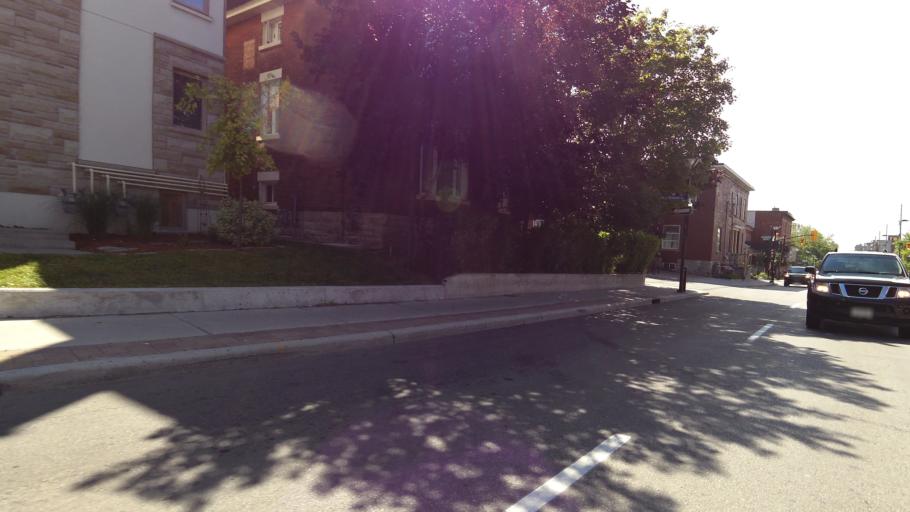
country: CA
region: Ontario
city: Ottawa
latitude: 45.4103
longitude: -75.7051
